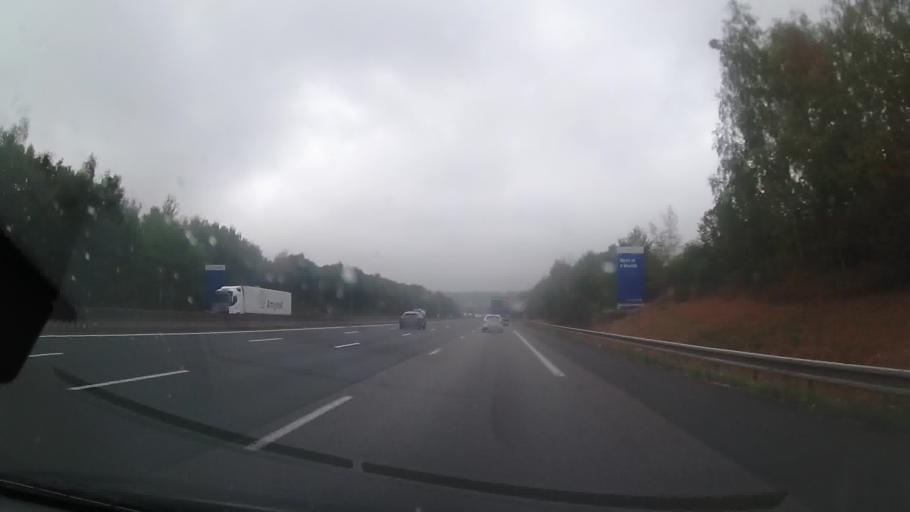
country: FR
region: Ile-de-France
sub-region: Departement de l'Essonne
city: Les Ulis
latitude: 48.6493
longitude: 2.1682
